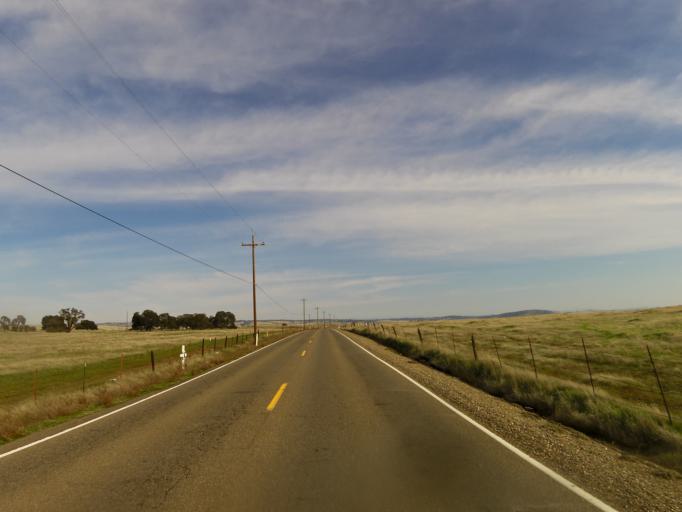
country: US
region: California
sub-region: Sacramento County
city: Folsom
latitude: 38.6184
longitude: -121.1374
